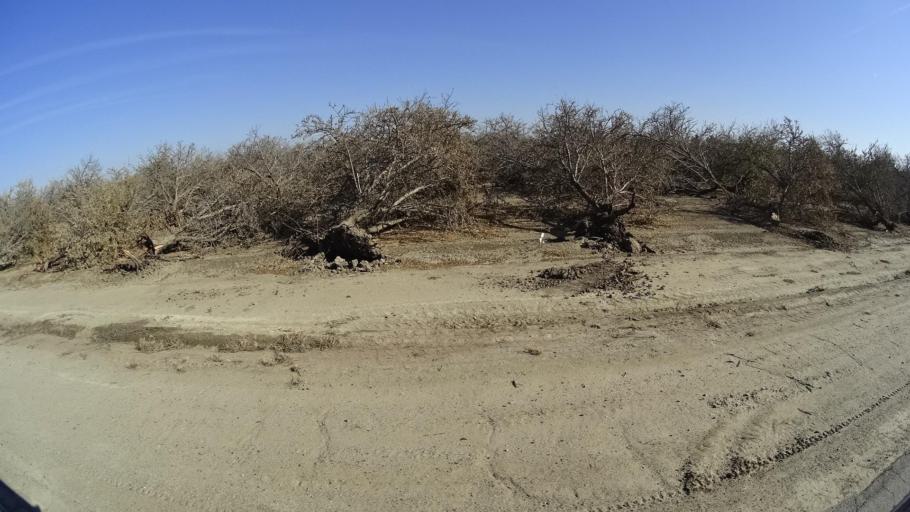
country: US
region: California
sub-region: Kern County
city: Wasco
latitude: 35.6623
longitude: -119.3486
